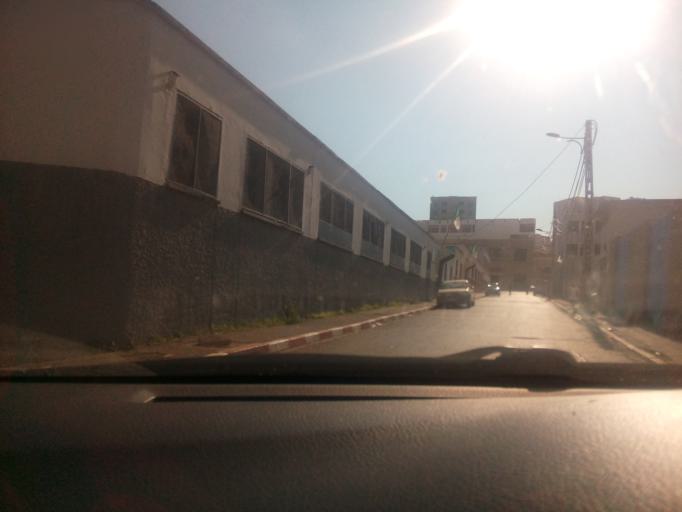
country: DZ
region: Oran
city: Oran
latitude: 35.7083
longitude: -0.6237
